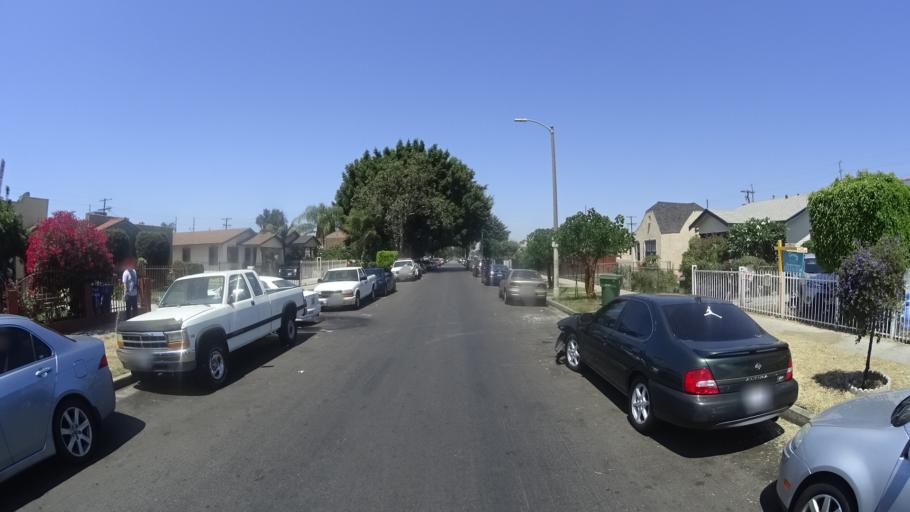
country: US
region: California
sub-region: Los Angeles County
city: Westmont
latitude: 33.9884
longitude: -118.2942
